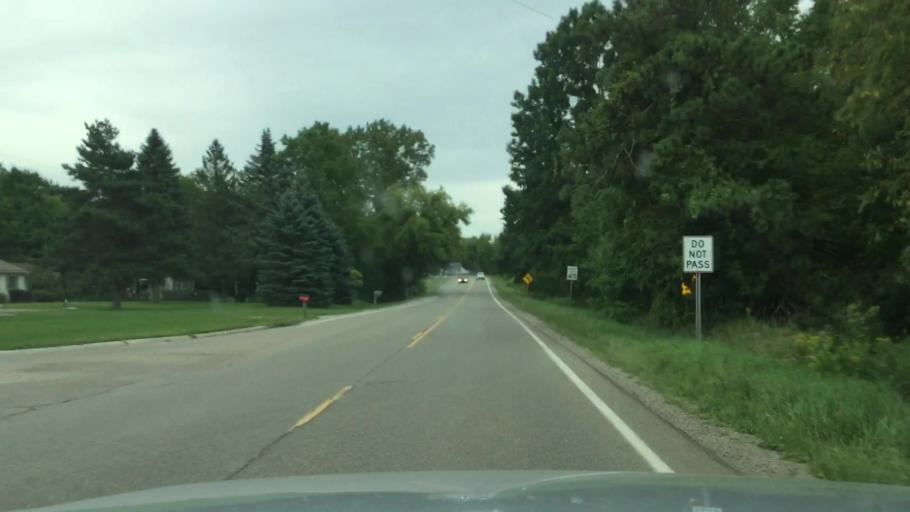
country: US
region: Michigan
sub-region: Genesee County
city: Argentine
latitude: 42.7946
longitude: -83.8548
